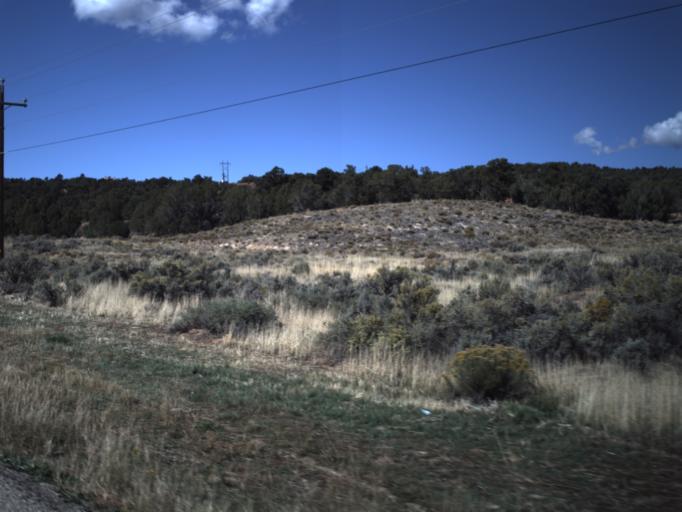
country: US
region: Utah
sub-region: Iron County
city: Cedar City
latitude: 37.6355
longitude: -113.2879
